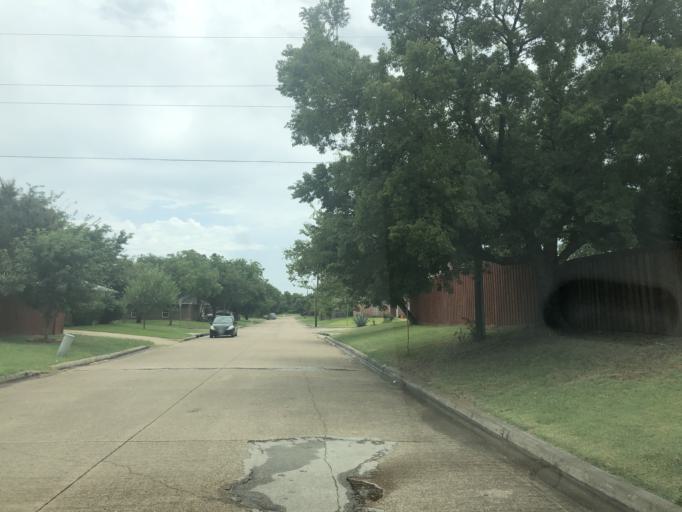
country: US
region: Texas
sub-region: Dallas County
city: Grand Prairie
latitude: 32.7496
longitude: -97.0375
